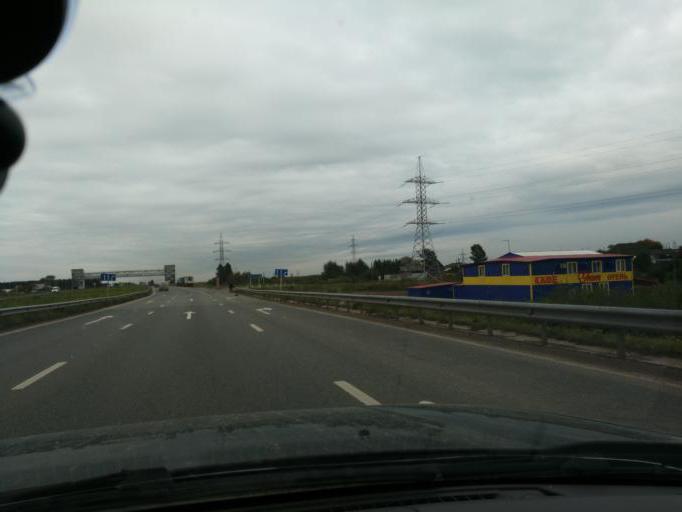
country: RU
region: Perm
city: Froly
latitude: 57.9344
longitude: 56.2355
